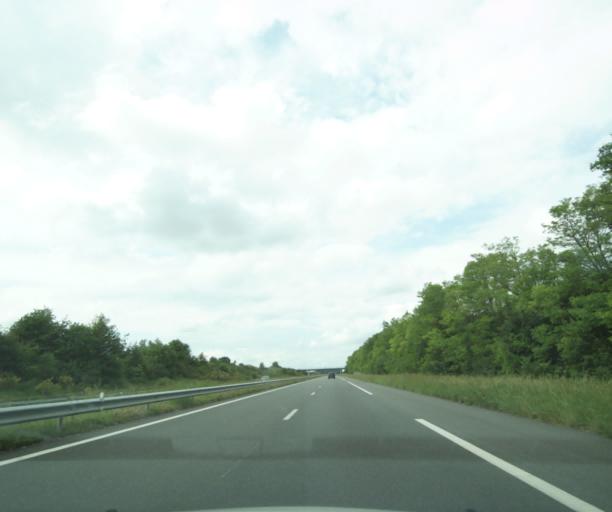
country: FR
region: Centre
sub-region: Departement du Cher
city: Orval
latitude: 46.7991
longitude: 2.4135
